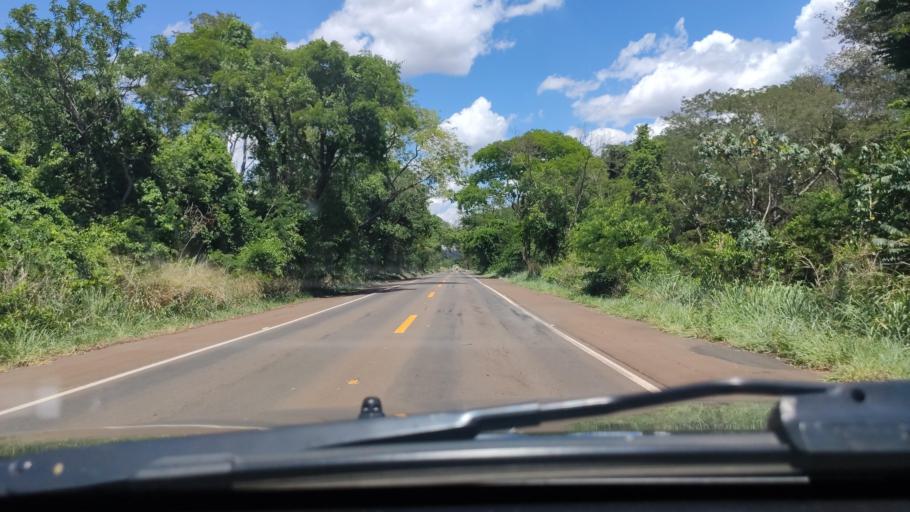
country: BR
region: Sao Paulo
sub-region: Boa Esperanca Do Sul
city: Boa Esperanca do Sul
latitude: -22.0697
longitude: -48.4187
